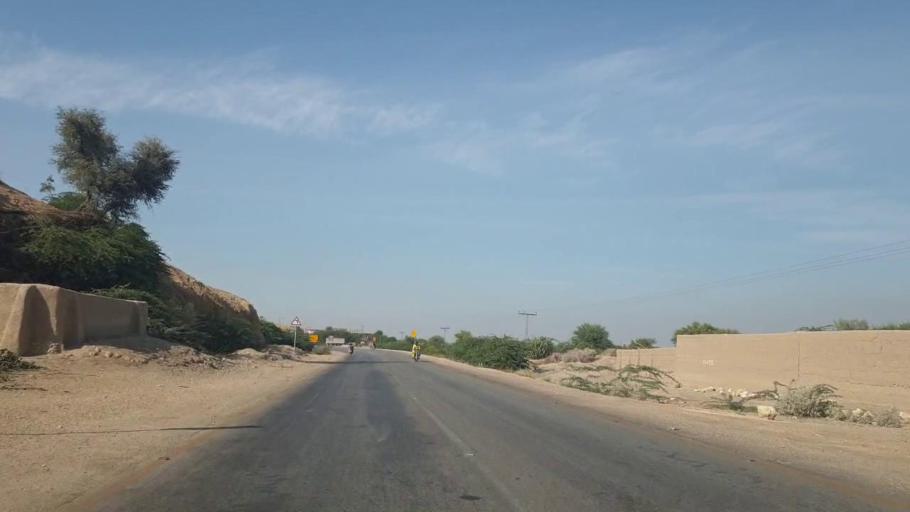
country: PK
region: Sindh
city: Sehwan
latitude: 26.3130
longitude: 67.8917
